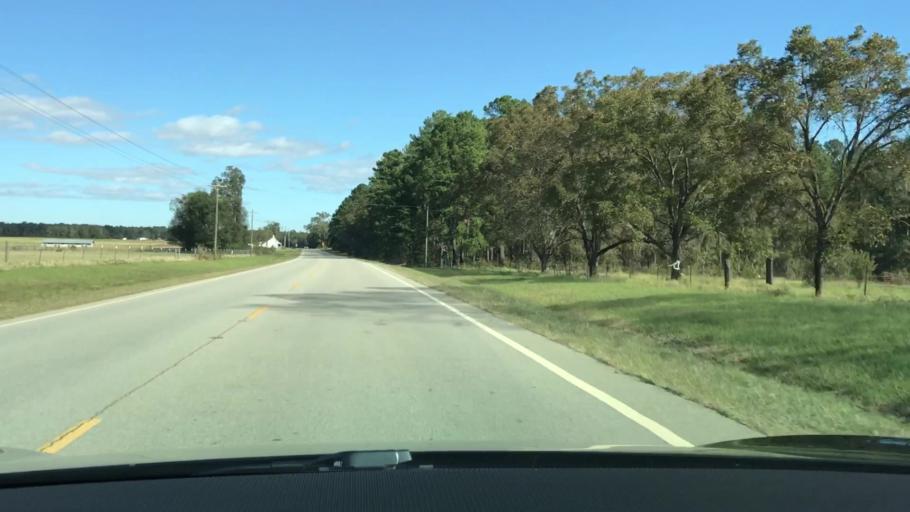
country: US
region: Georgia
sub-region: Jefferson County
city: Wrens
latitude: 33.1721
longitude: -82.4542
